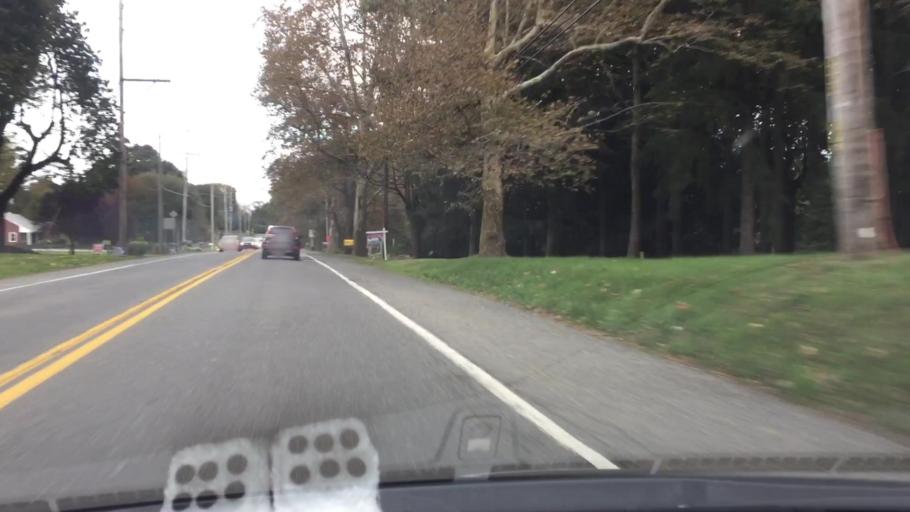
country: US
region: Pennsylvania
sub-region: Delaware County
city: Chester Heights
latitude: 39.9434
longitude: -75.4938
